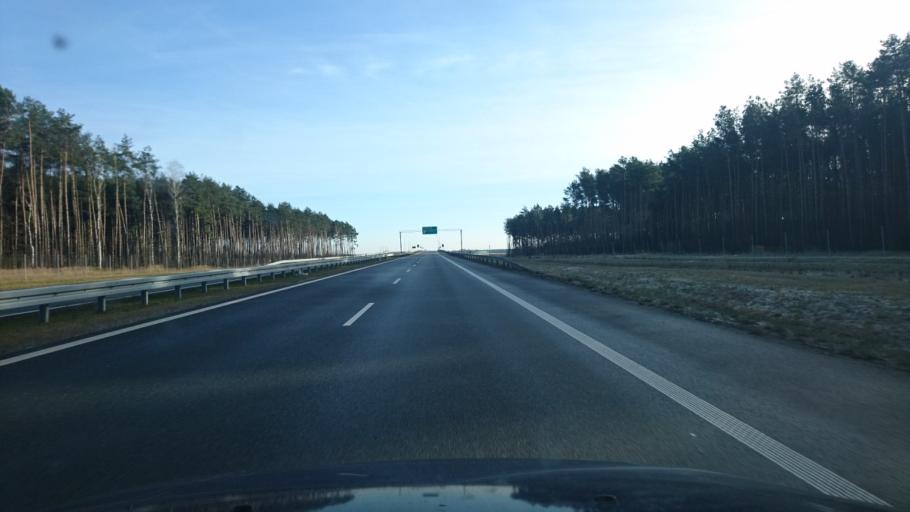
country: PL
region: Greater Poland Voivodeship
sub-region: Powiat kepinski
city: Kepno
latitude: 51.3257
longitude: 17.9910
